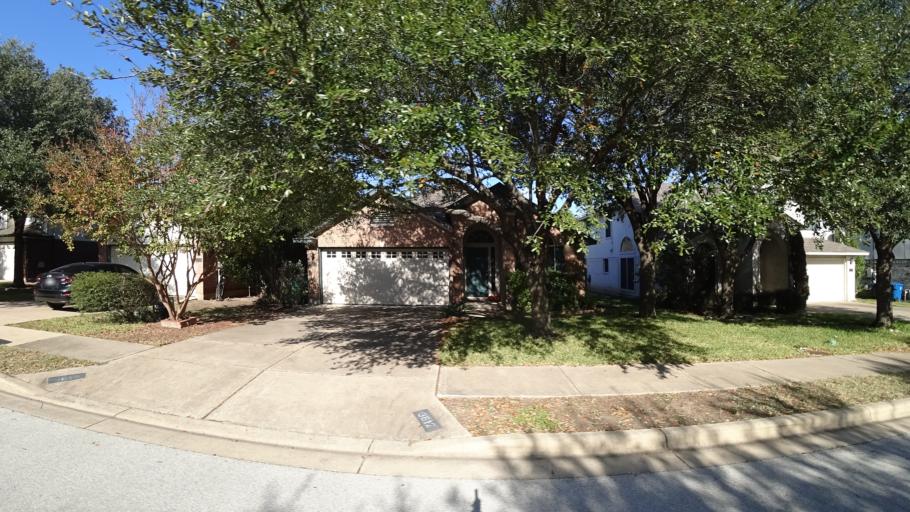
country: US
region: Texas
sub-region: Travis County
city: Wells Branch
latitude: 30.4609
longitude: -97.6840
